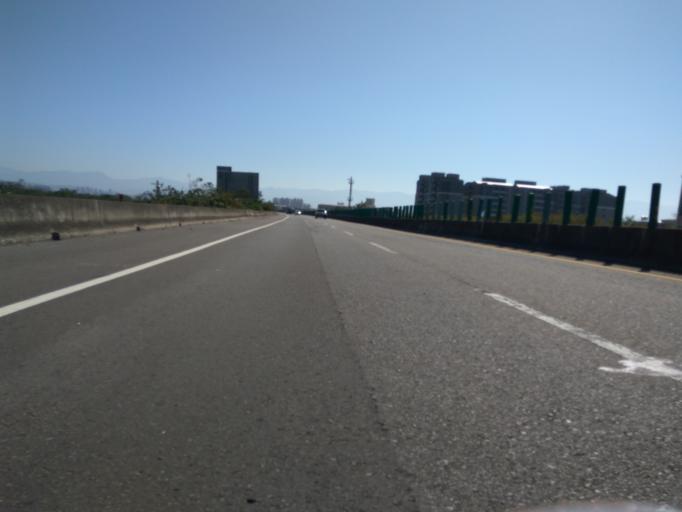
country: TW
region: Taiwan
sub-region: Hsinchu
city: Hsinchu
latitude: 24.8375
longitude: 120.9454
